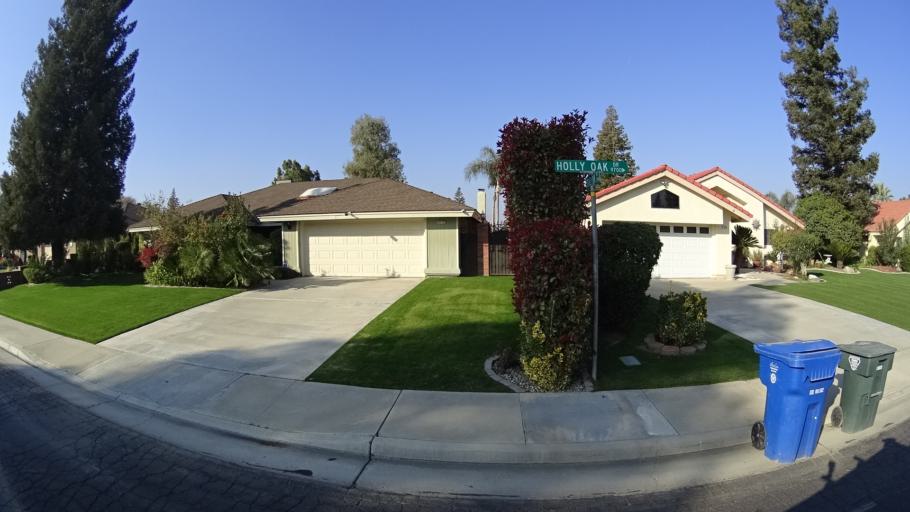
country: US
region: California
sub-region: Kern County
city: Greenacres
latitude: 35.3322
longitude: -119.1105
